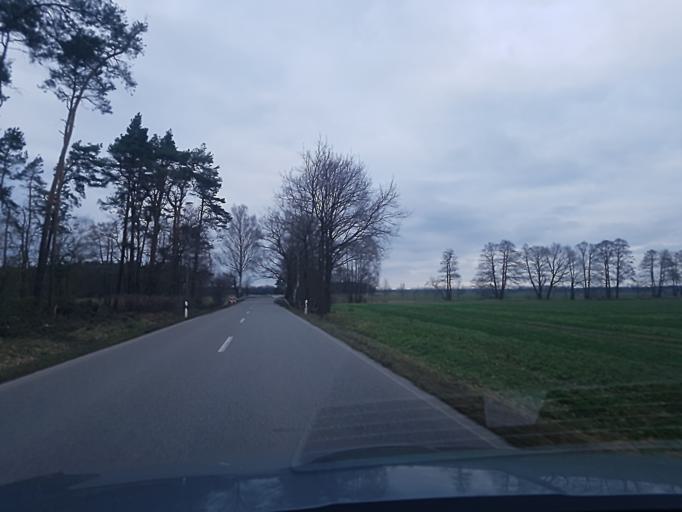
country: DE
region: Brandenburg
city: Finsterwalde
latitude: 51.6678
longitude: 13.6924
